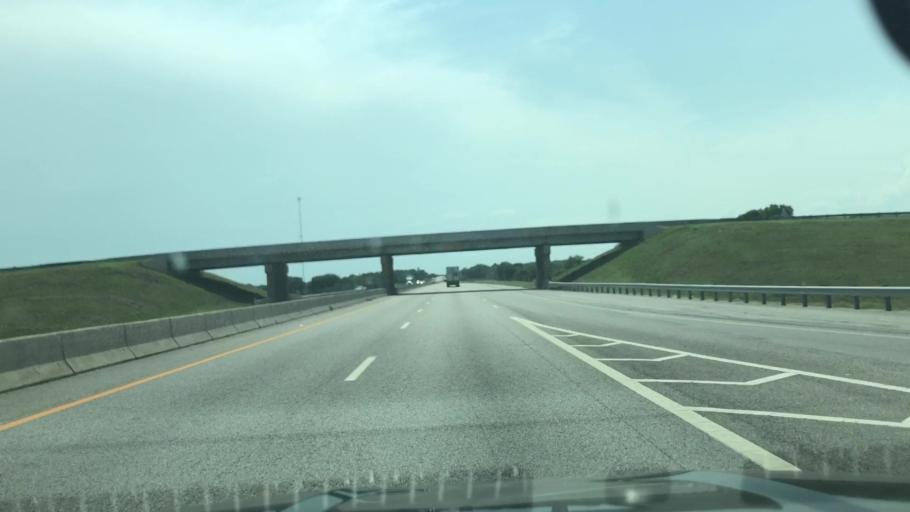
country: US
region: Oklahoma
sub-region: Ottawa County
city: Afton
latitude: 36.7227
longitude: -94.9346
